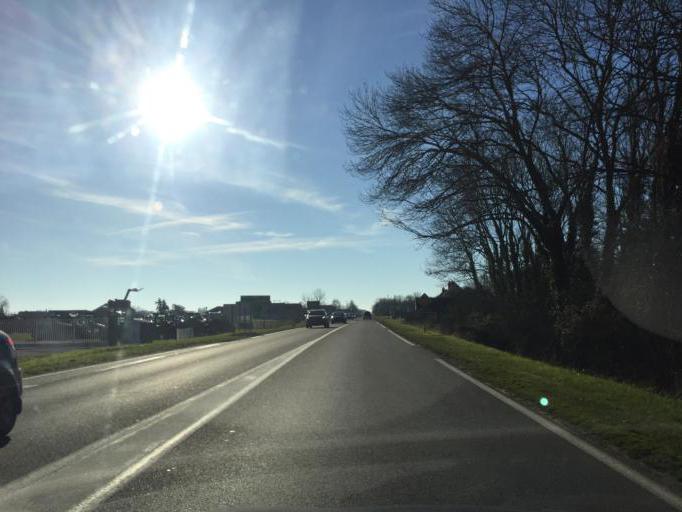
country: FR
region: Auvergne
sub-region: Departement de l'Allier
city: Saint-Pourcain-sur-Sioule
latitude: 46.2974
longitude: 3.2954
